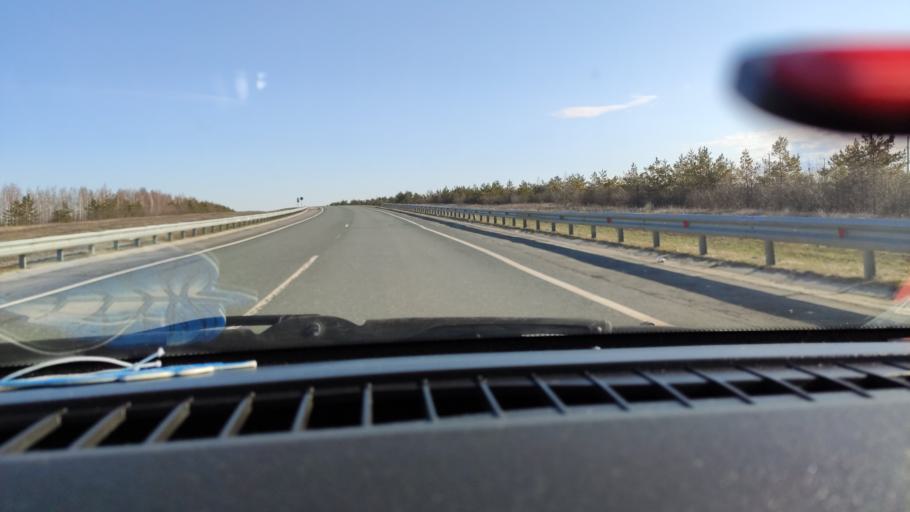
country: RU
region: Samara
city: Syzran'
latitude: 52.8760
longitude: 48.2897
